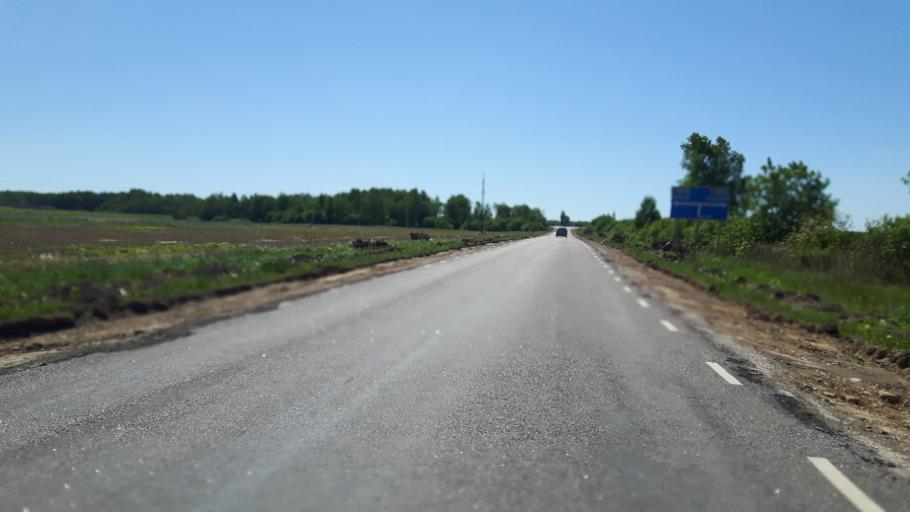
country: EE
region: Ida-Virumaa
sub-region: Narva-Joesuu linn
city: Narva-Joesuu
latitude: 59.3830
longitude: 27.9210
